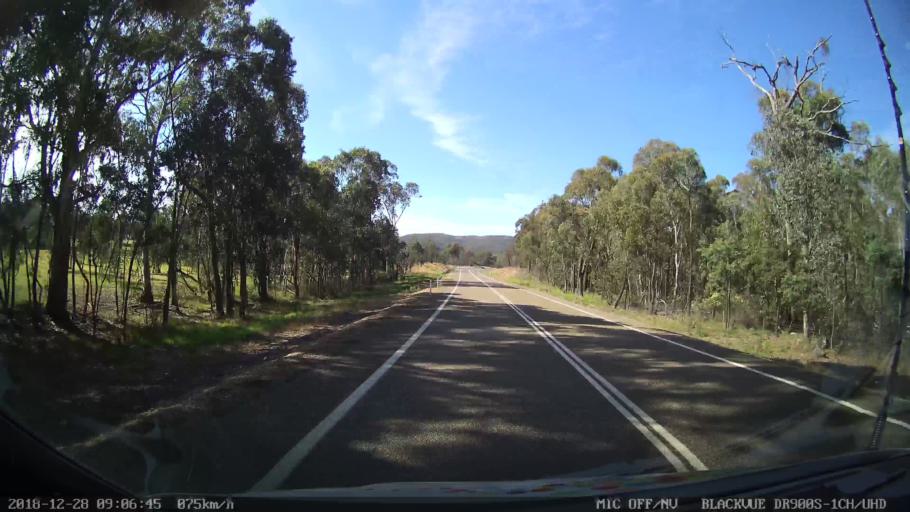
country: AU
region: New South Wales
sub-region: Upper Lachlan Shire
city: Crookwell
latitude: -34.1995
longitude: 149.3461
